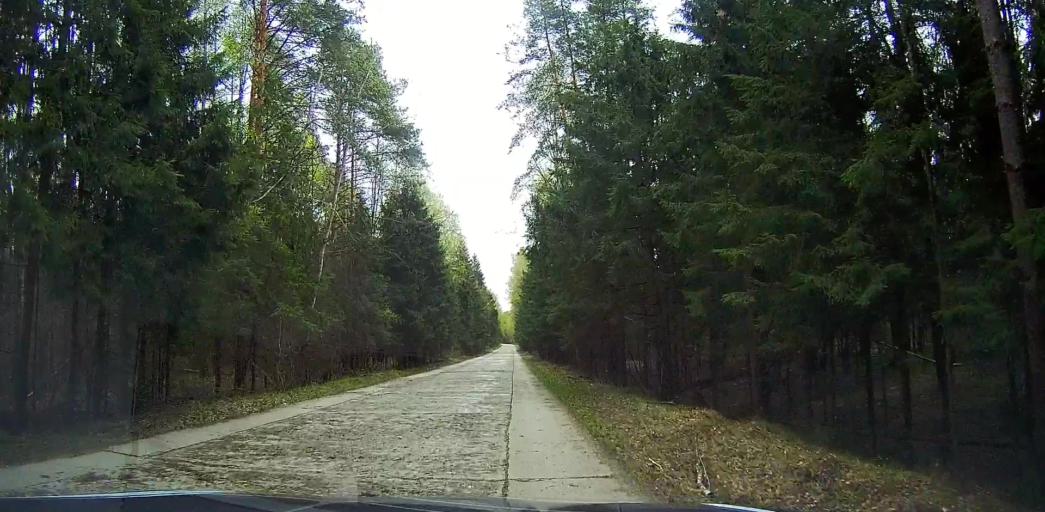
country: RU
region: Moskovskaya
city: Malyshevo
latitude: 55.5369
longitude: 38.3838
